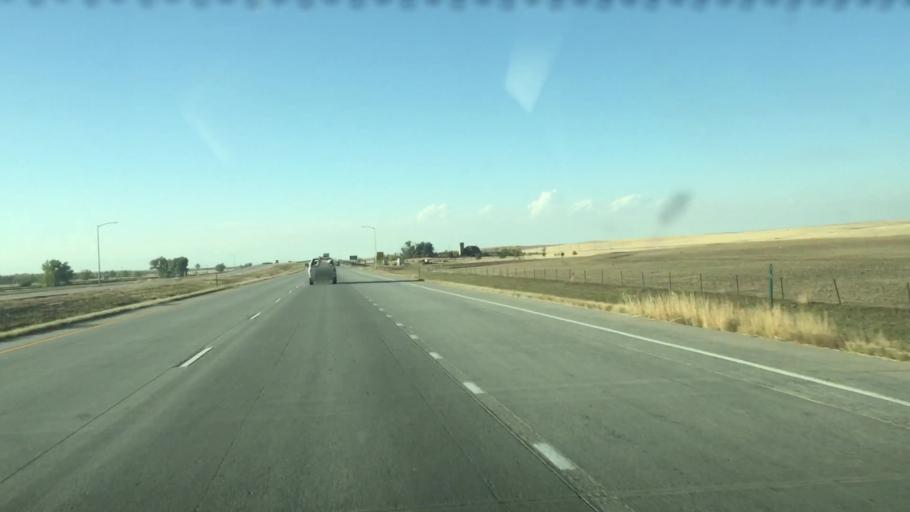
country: US
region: Colorado
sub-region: Arapahoe County
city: Byers
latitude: 39.5012
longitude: -103.9686
